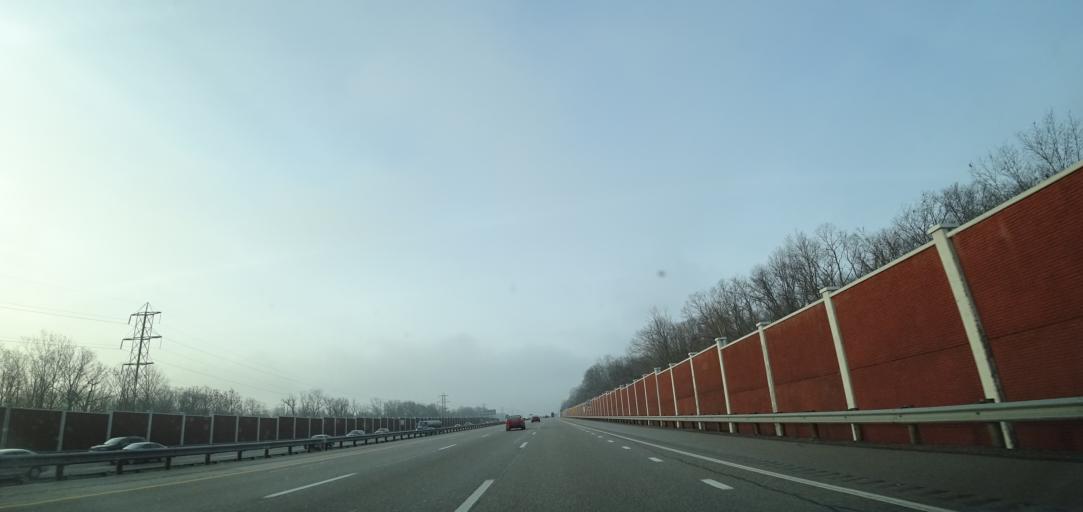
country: US
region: Ohio
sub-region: Cuyahoga County
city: Independence
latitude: 41.3550
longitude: -81.6495
